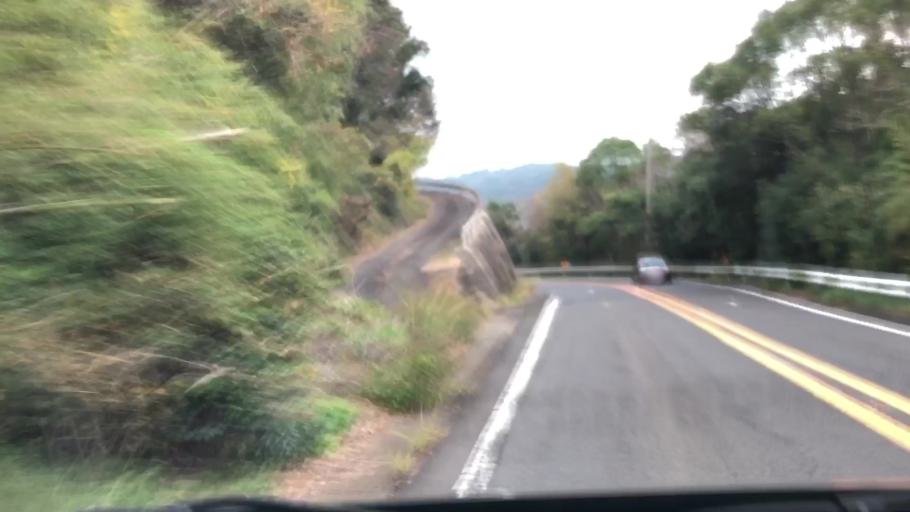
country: JP
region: Nagasaki
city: Sasebo
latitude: 33.0472
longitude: 129.7168
